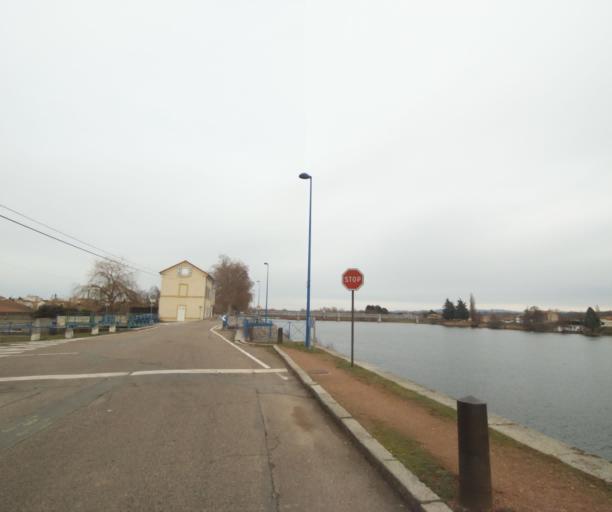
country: FR
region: Rhone-Alpes
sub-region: Departement de la Loire
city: Le Coteau
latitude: 46.0348
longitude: 4.0815
